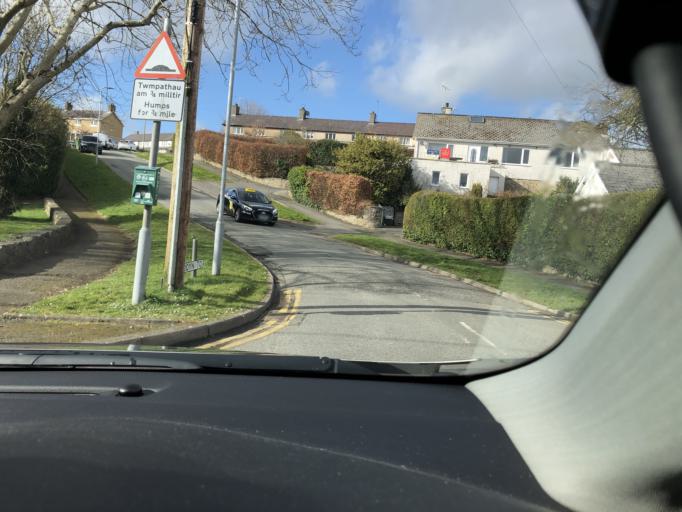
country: GB
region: Wales
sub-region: Anglesey
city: Menai Bridge
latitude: 53.2273
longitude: -4.1669
